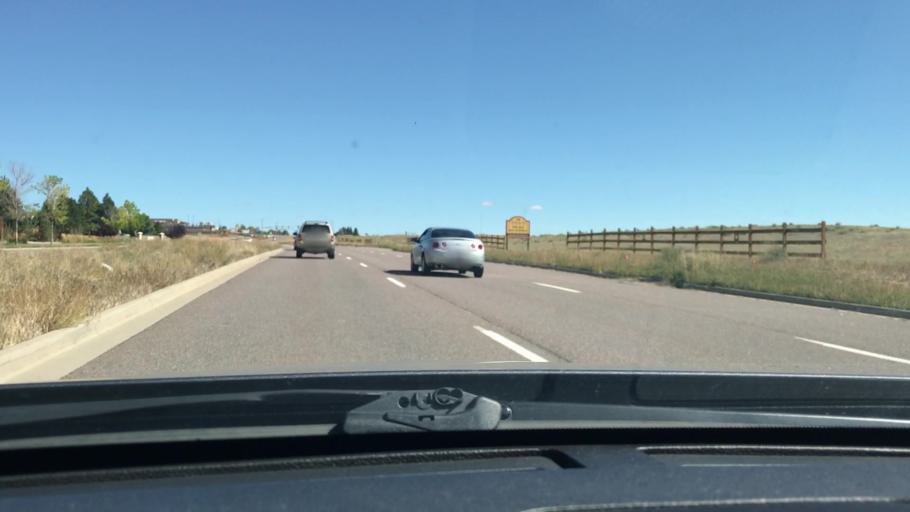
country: US
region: Colorado
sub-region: Arapahoe County
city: Dove Valley
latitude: 39.6384
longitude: -104.7442
